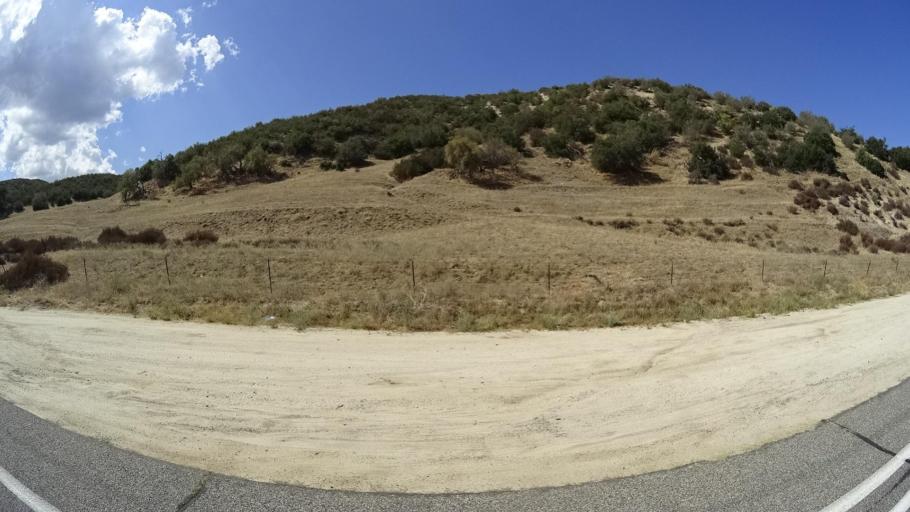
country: US
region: California
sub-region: San Diego County
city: Julian
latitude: 33.2361
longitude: -116.6516
